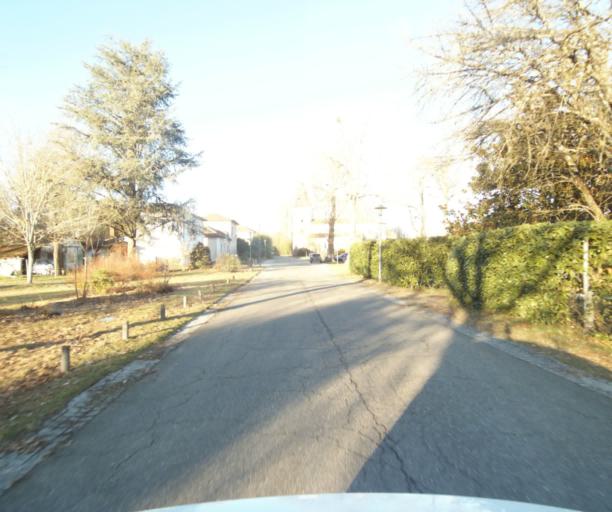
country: FR
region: Aquitaine
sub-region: Departement des Landes
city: Gabarret
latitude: 44.1080
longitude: -0.1029
